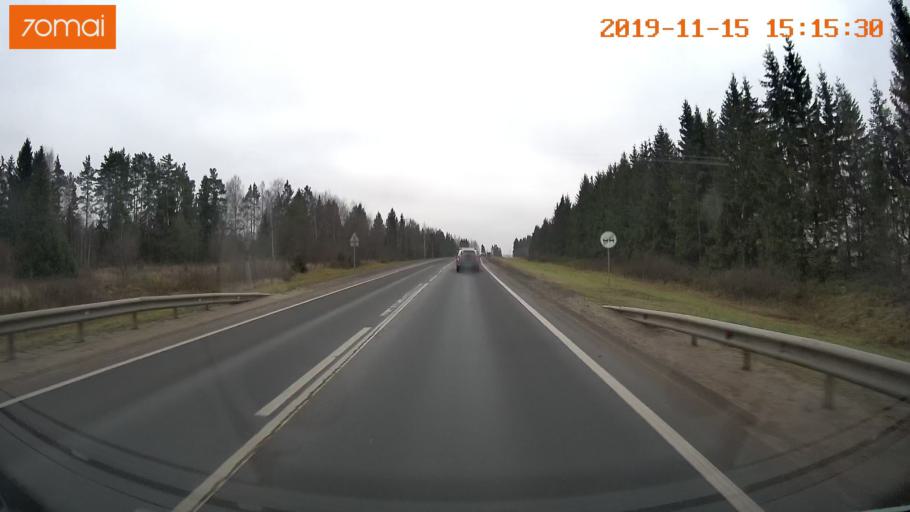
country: RU
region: Jaroslavl
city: Danilov
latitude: 58.2838
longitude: 40.1989
